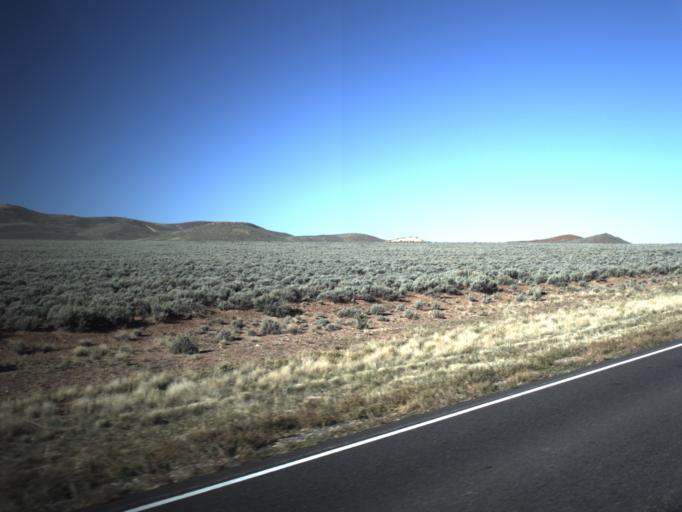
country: US
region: Utah
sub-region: Washington County
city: Enterprise
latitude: 37.7319
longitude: -113.7186
